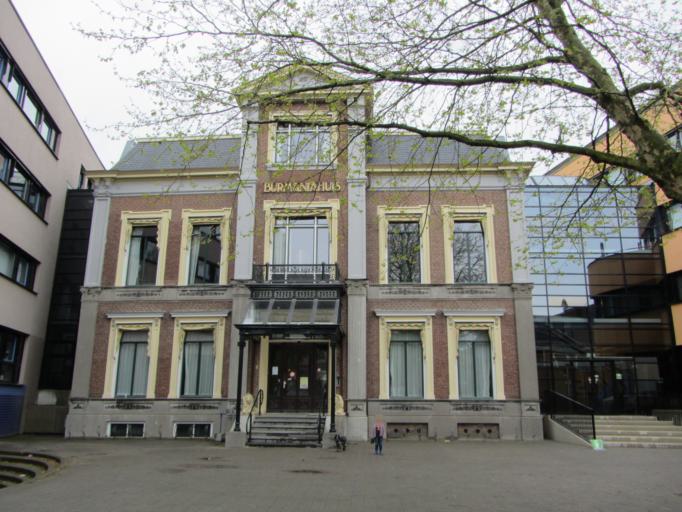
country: NL
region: Friesland
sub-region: Gemeente Leeuwarden
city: Bilgaard
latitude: 53.2018
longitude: 5.7900
